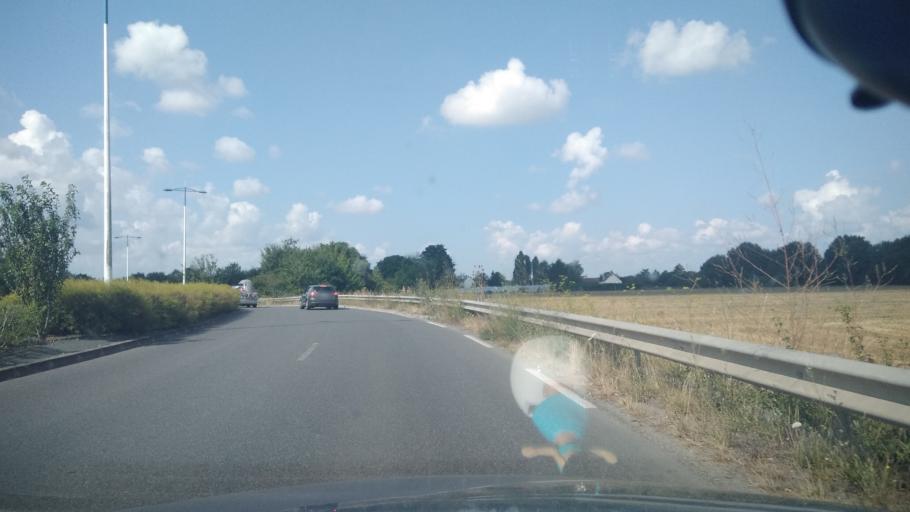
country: FR
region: Centre
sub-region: Departement d'Indre-et-Loire
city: Chambray-les-Tours
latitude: 47.3328
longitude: 0.6853
